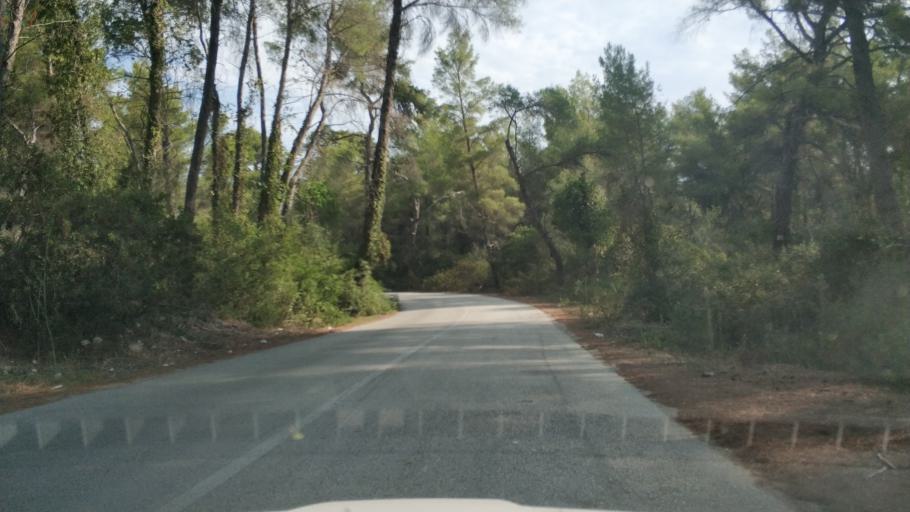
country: AL
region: Fier
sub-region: Rrethi i Lushnjes
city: Divjake
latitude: 40.9866
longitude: 19.4836
